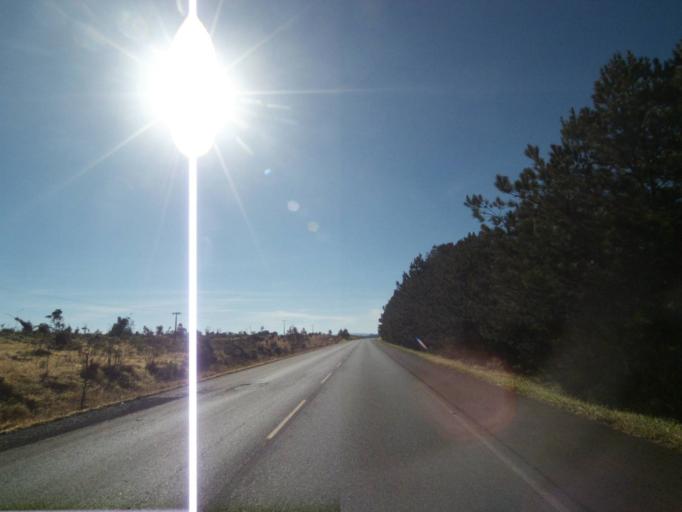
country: BR
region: Parana
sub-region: Tibagi
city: Tibagi
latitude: -24.4336
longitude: -50.4151
